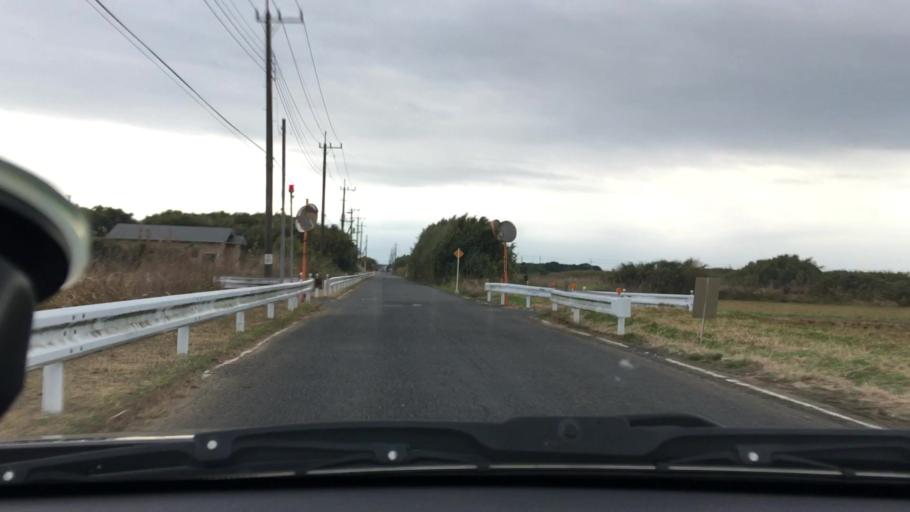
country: JP
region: Chiba
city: Omigawa
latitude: 35.8799
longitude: 140.6752
